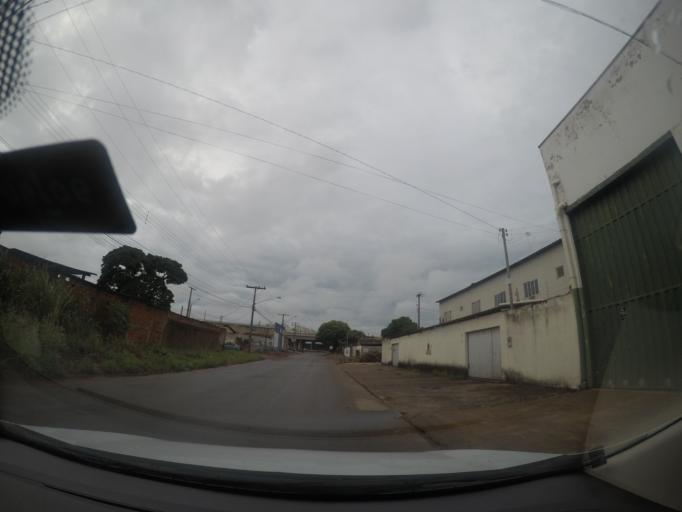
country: BR
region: Goias
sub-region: Goiania
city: Goiania
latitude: -16.6993
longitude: -49.3346
